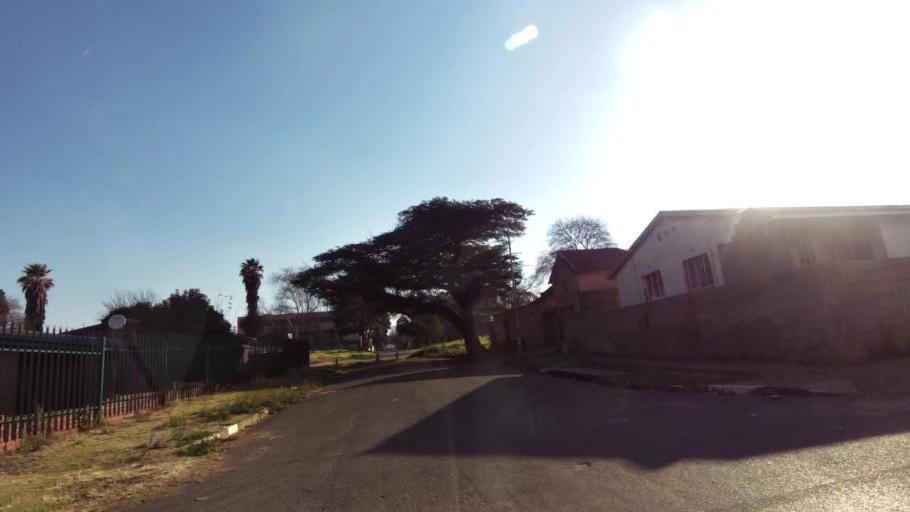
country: ZA
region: Gauteng
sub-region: City of Johannesburg Metropolitan Municipality
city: Johannesburg
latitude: -26.1932
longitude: 28.0189
